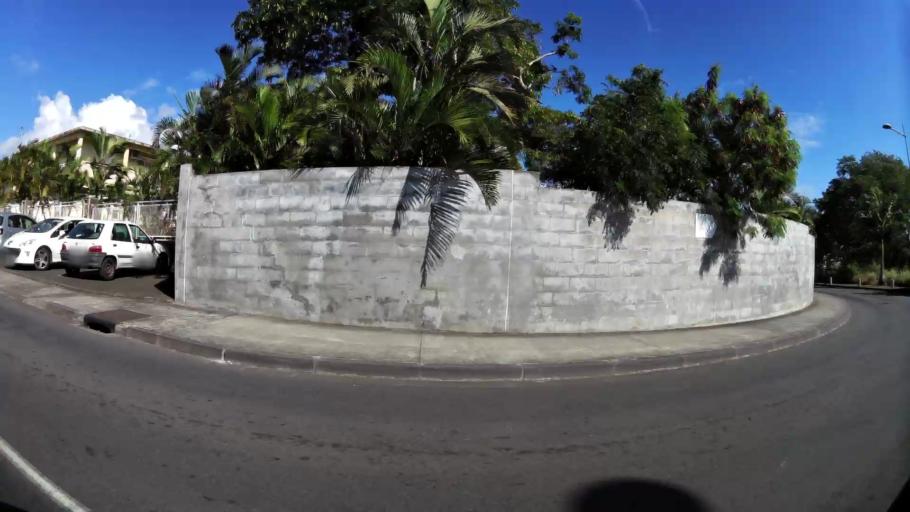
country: RE
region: Reunion
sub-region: Reunion
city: Sainte-Marie
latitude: -20.8969
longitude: 55.5012
